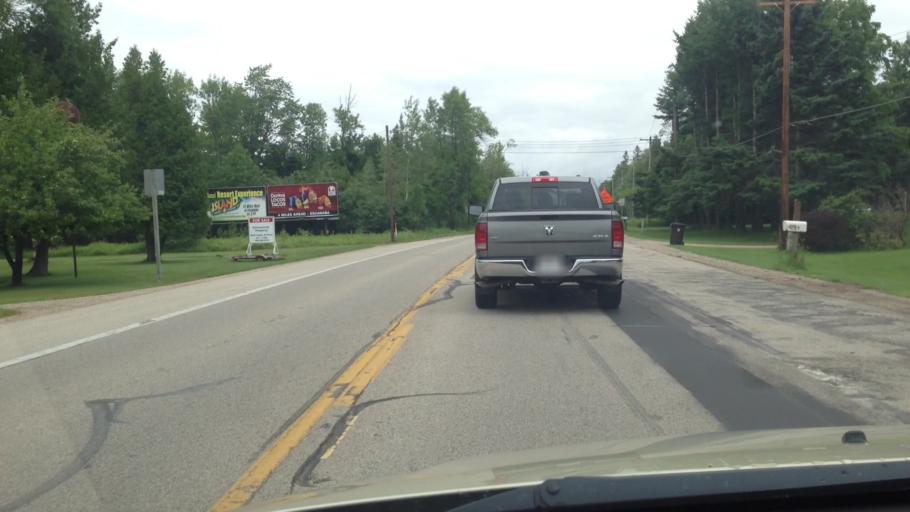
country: US
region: Michigan
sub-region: Delta County
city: Escanaba
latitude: 45.6980
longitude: -87.1015
